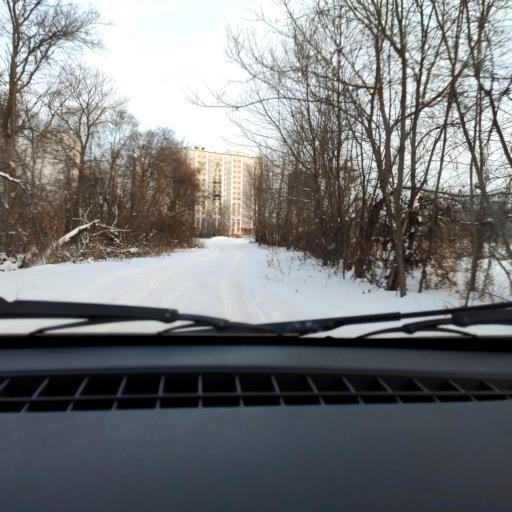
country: RU
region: Bashkortostan
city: Mikhaylovka
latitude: 54.7879
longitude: 55.8465
